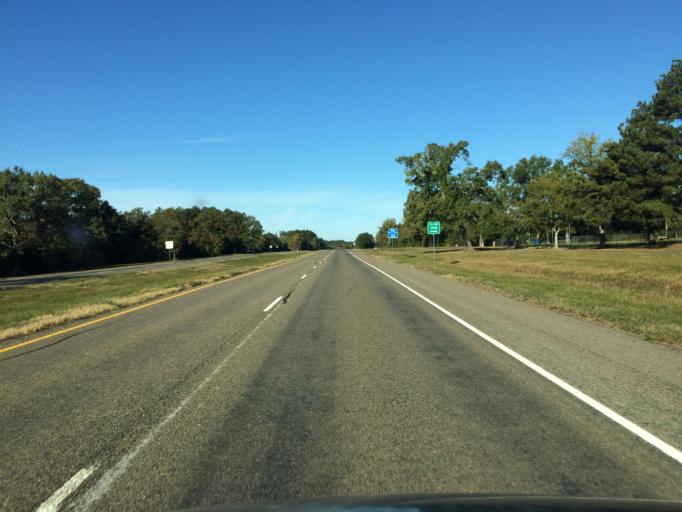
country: US
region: Texas
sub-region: Wood County
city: Hawkins
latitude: 32.5957
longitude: -95.2442
